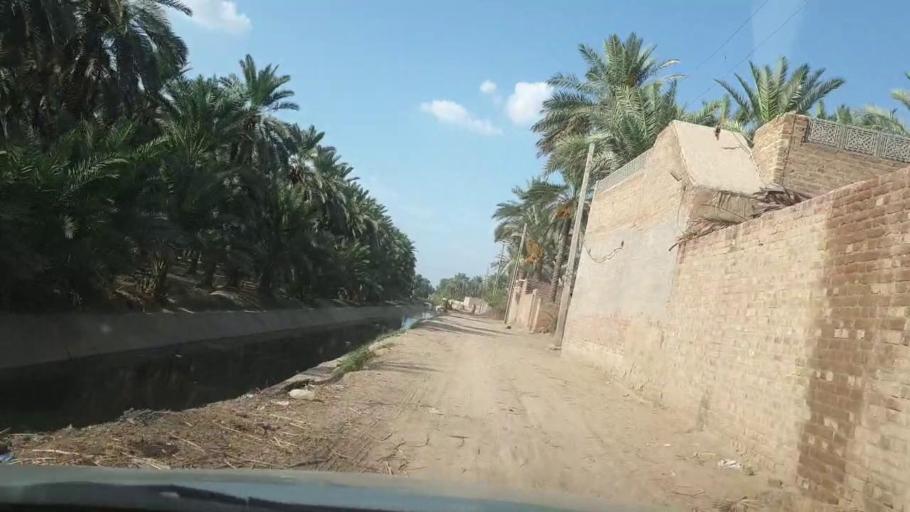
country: PK
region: Sindh
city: Sukkur
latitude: 27.6541
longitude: 68.8303
